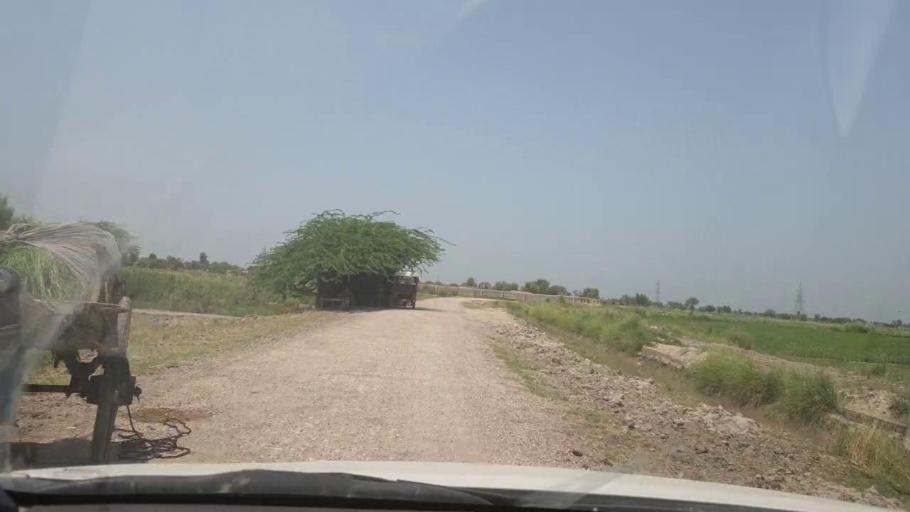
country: PK
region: Sindh
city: Lakhi
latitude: 27.8705
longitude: 68.6944
